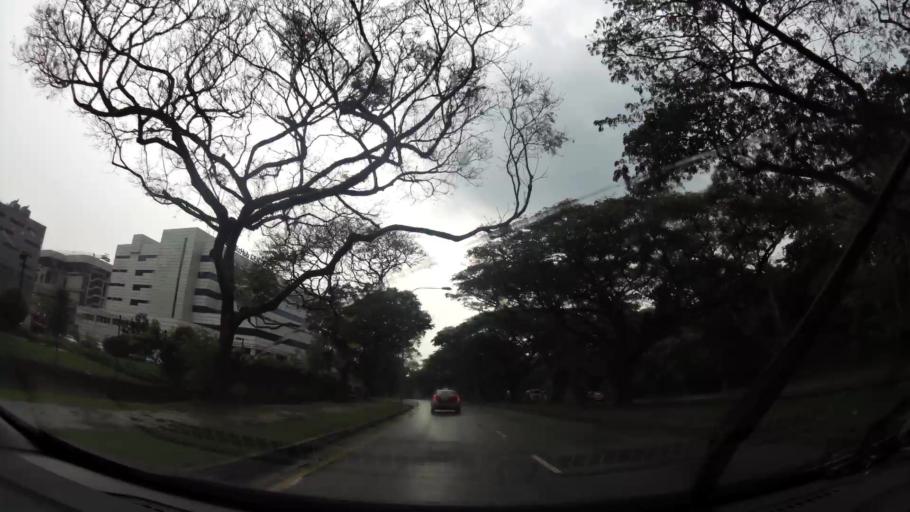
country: MY
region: Johor
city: Kampung Pasir Gudang Baru
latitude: 1.3915
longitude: 103.8471
